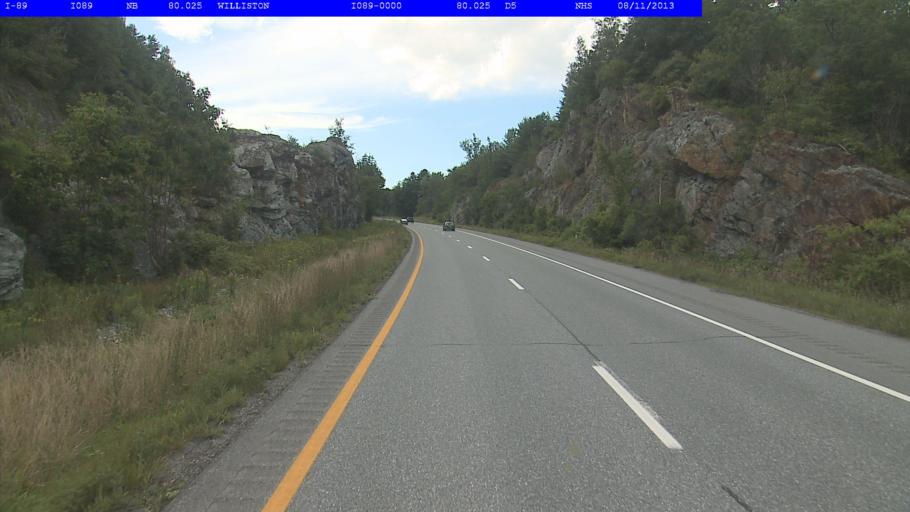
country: US
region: Vermont
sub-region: Chittenden County
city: Williston
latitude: 44.4304
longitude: -73.0375
